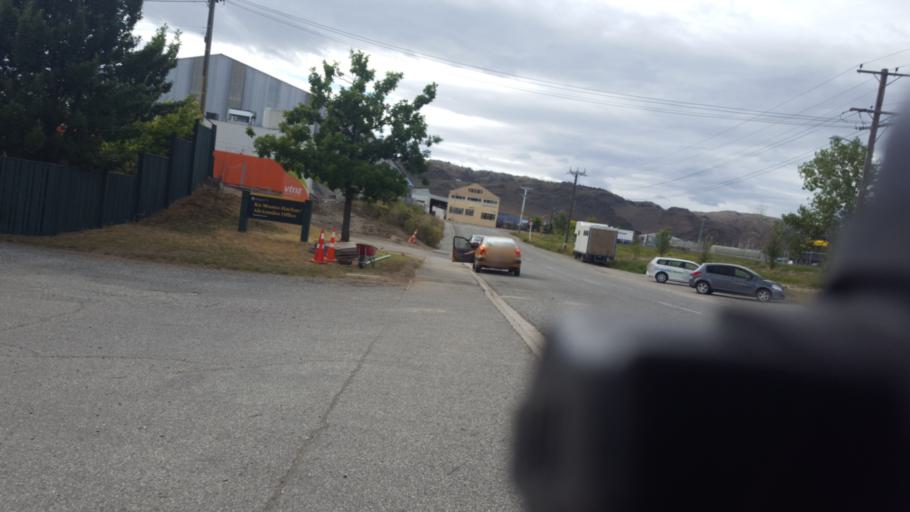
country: NZ
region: Otago
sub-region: Queenstown-Lakes District
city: Wanaka
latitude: -45.2446
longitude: 169.3943
